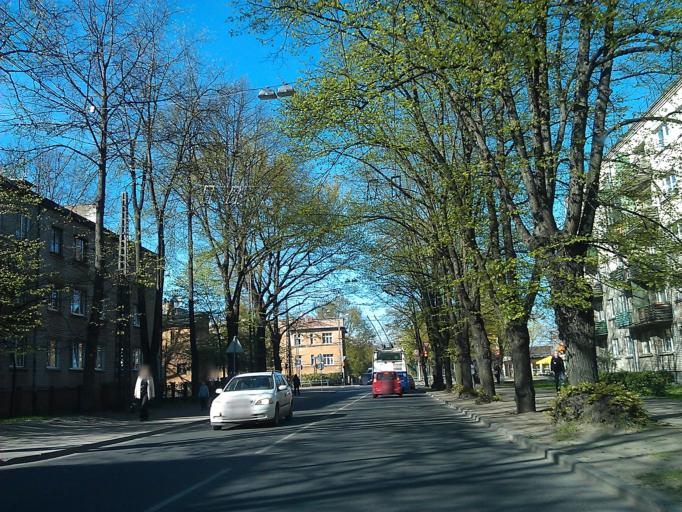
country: LV
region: Riga
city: Jaunciems
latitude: 56.9699
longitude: 24.1780
